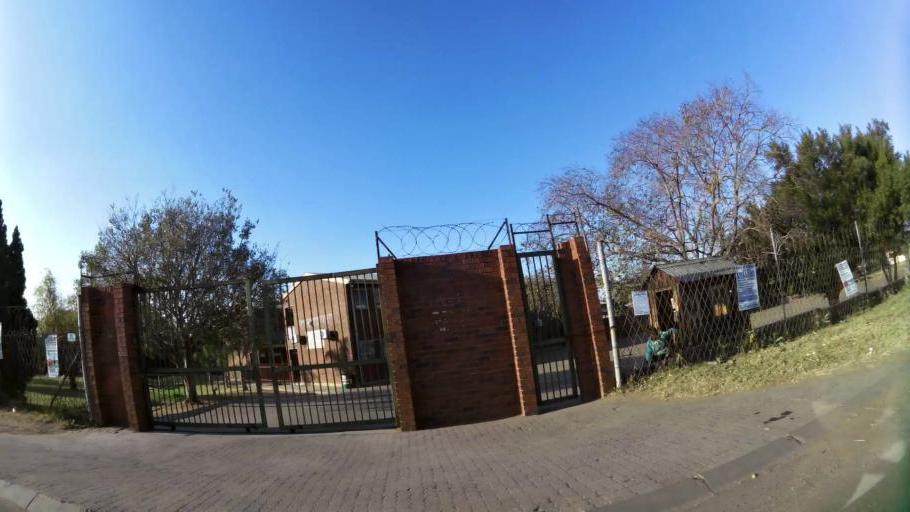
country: ZA
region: North-West
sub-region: Bojanala Platinum District Municipality
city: Rustenburg
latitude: -25.6438
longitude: 27.2272
